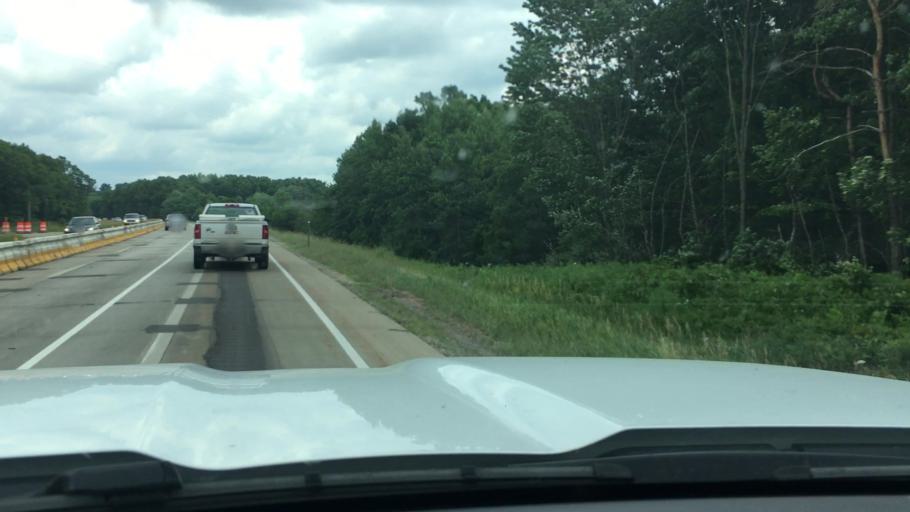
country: US
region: Michigan
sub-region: Kent County
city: Rockford
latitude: 43.1310
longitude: -85.5952
